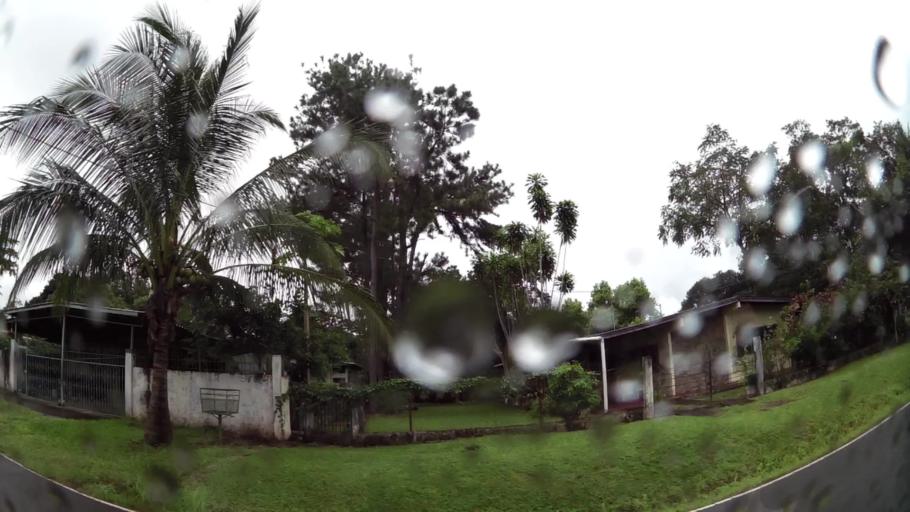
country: PA
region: Chiriqui
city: David
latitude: 8.4328
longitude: -82.4404
